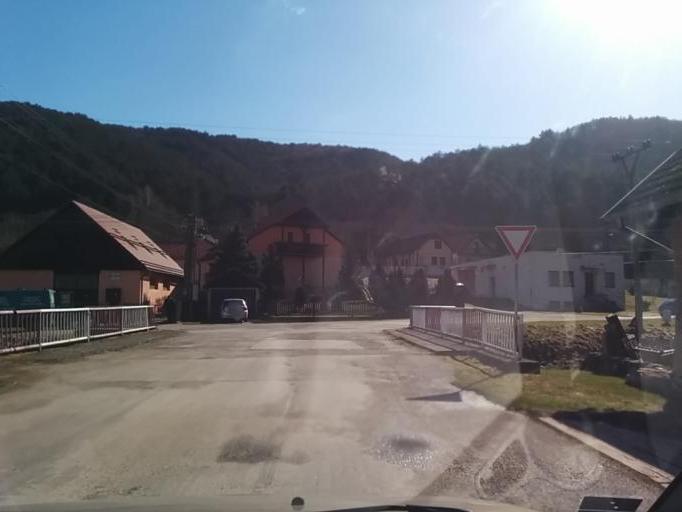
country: SK
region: Nitriansky
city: Cachtice
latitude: 48.7138
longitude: 17.7271
